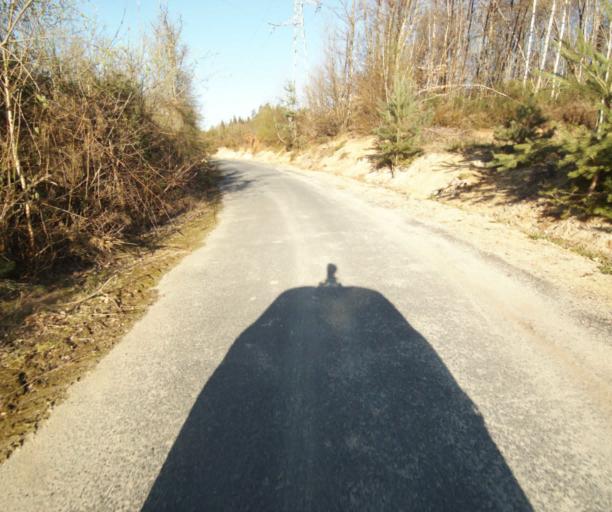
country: FR
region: Limousin
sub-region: Departement de la Correze
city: Correze
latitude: 45.3384
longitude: 1.9027
